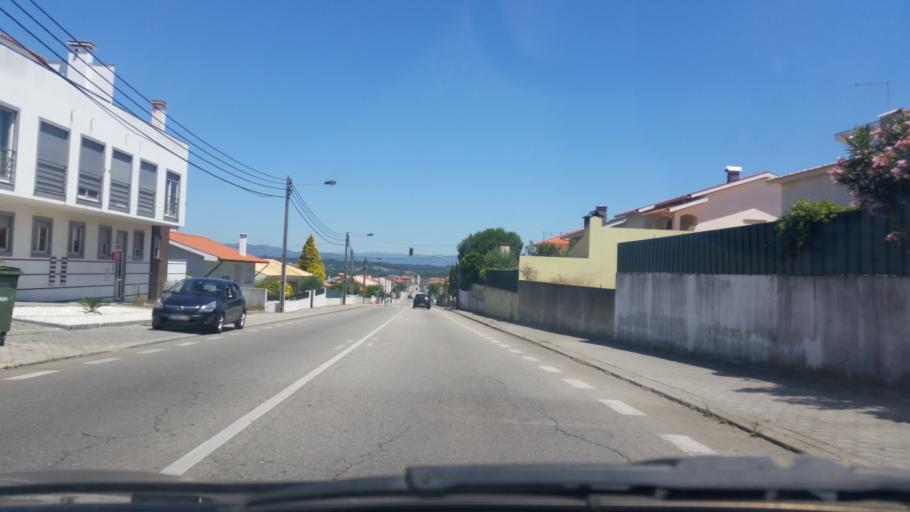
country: PT
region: Aveiro
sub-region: Aveiro
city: Oliveirinha
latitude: 40.6378
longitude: -8.5997
